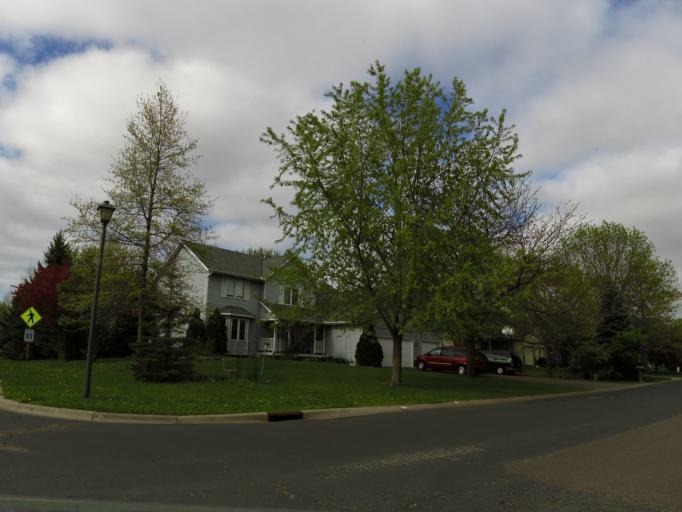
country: US
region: Minnesota
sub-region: Washington County
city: Woodbury
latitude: 44.9262
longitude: -92.9172
